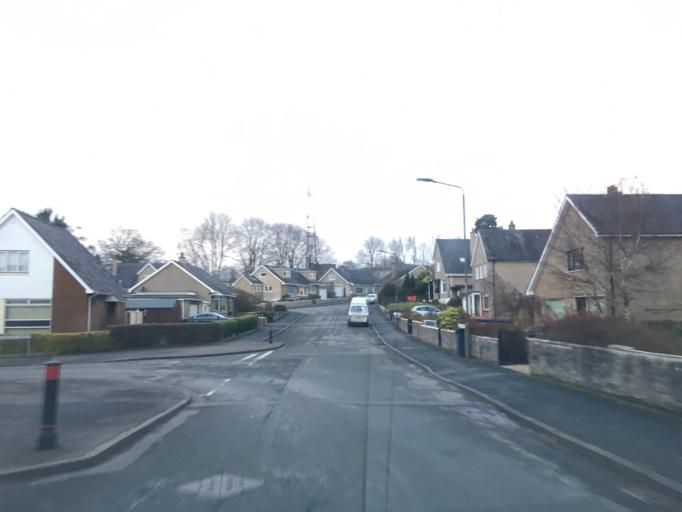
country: GB
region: Scotland
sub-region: Stirling
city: Stirling
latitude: 56.1080
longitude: -3.9432
